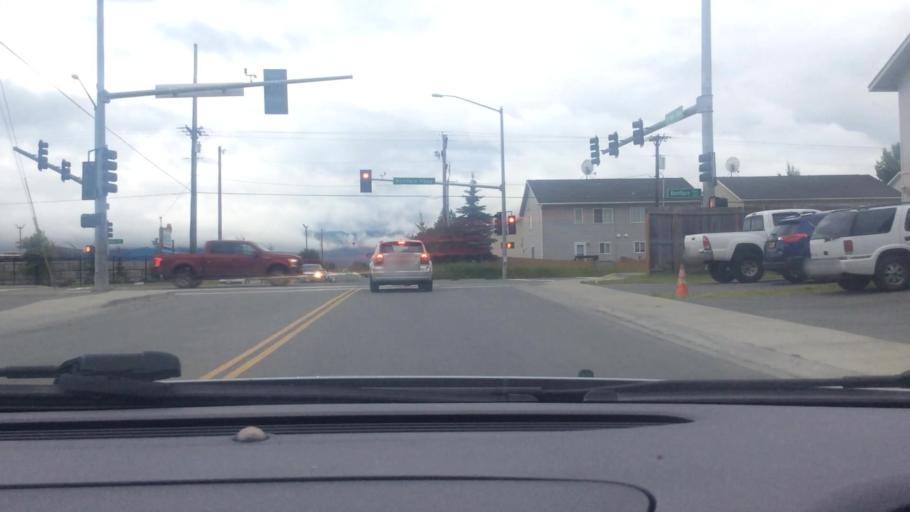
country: US
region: Alaska
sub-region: Anchorage Municipality
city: Anchorage
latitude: 61.2187
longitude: -149.7794
